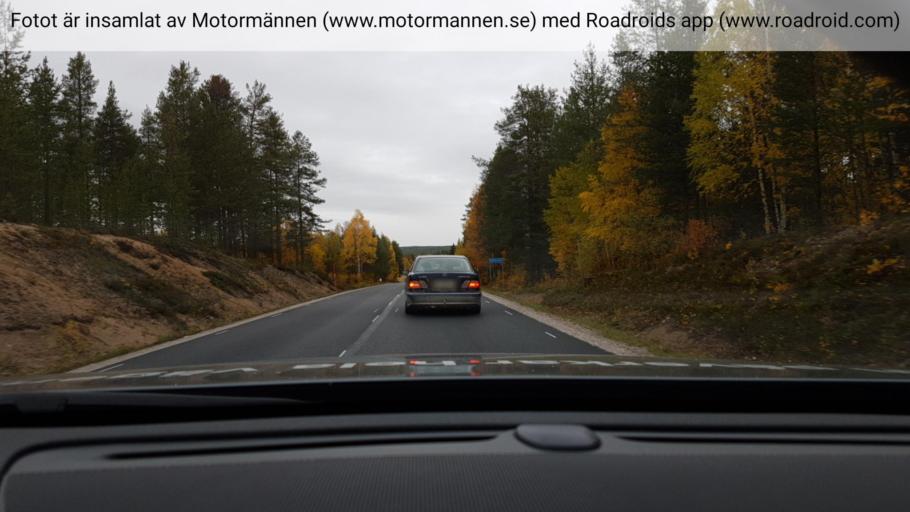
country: SE
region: Norrbotten
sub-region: Overkalix Kommun
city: OEverkalix
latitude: 66.4469
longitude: 22.7864
